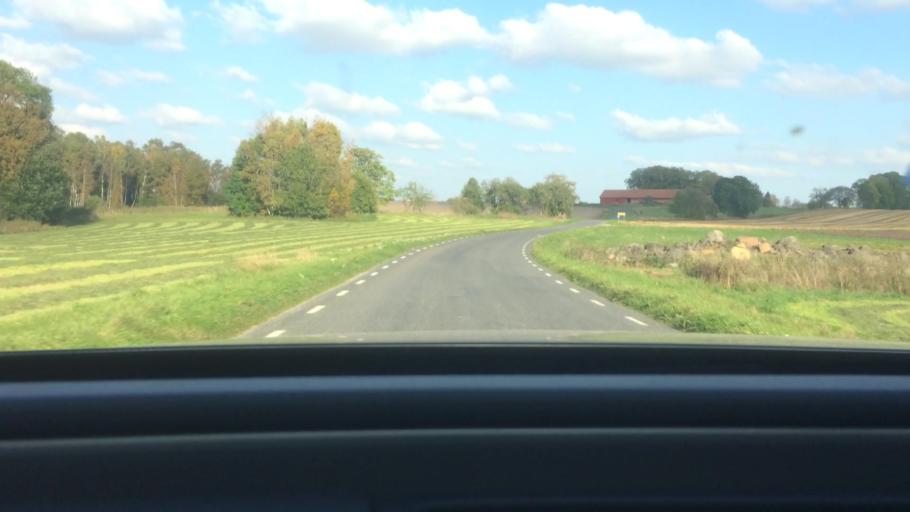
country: SE
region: Vaestra Goetaland
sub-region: Falkopings Kommun
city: Falkoeping
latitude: 58.1401
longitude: 13.5359
